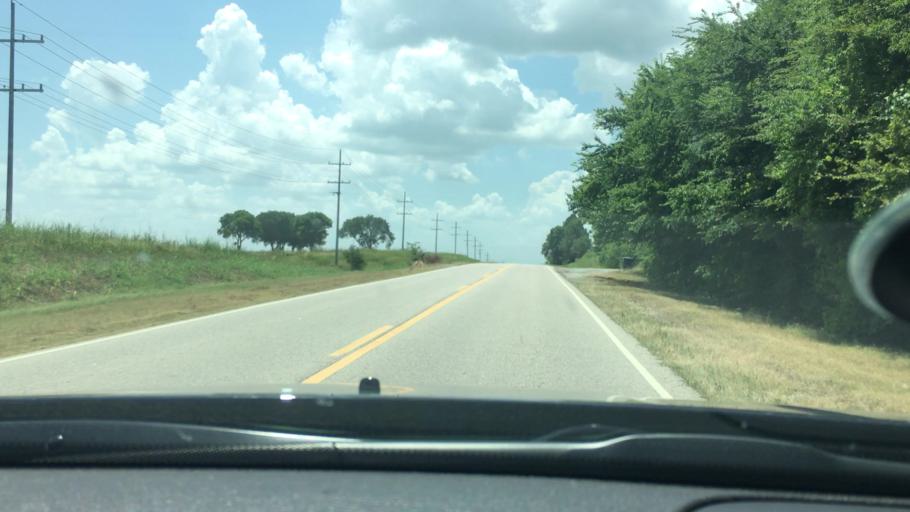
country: US
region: Oklahoma
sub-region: Pontotoc County
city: Ada
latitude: 34.6755
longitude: -96.6349
